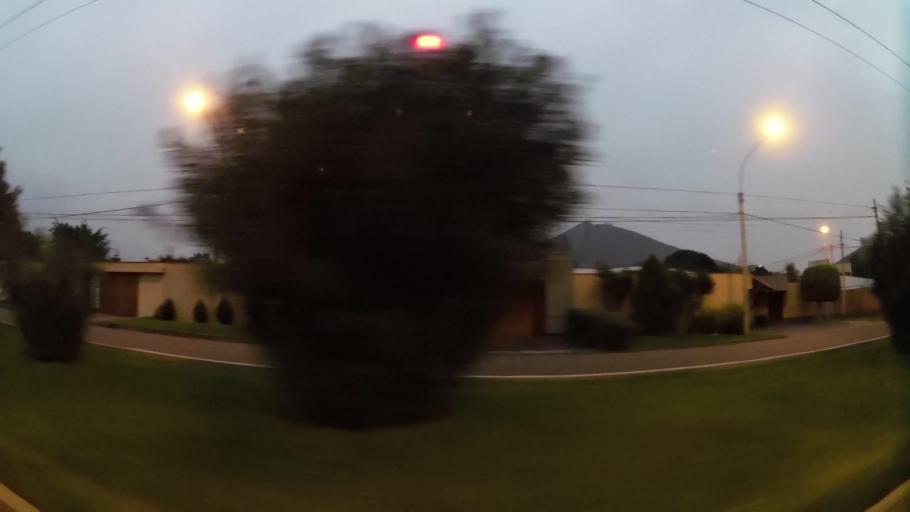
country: PE
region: Lima
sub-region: Lima
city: La Molina
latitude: -12.0873
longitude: -76.9534
